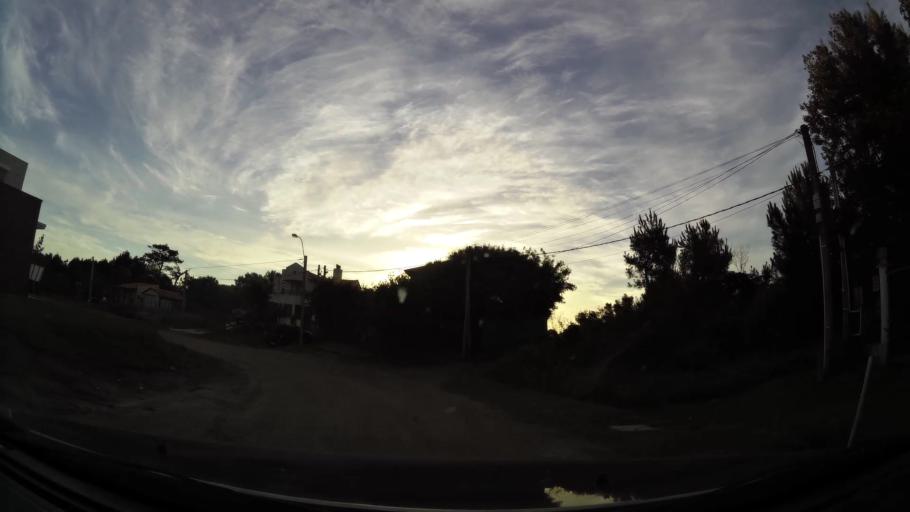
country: UY
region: Canelones
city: Atlantida
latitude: -34.7685
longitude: -55.7795
